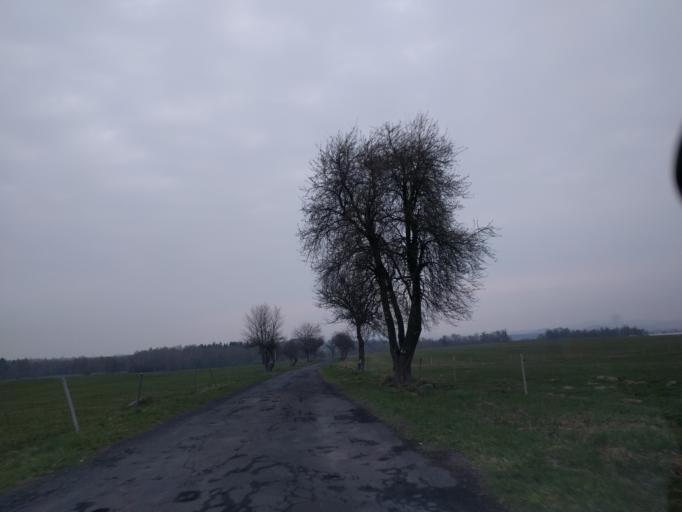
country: CZ
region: Karlovarsky
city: Bochov
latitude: 50.1224
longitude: 13.0852
